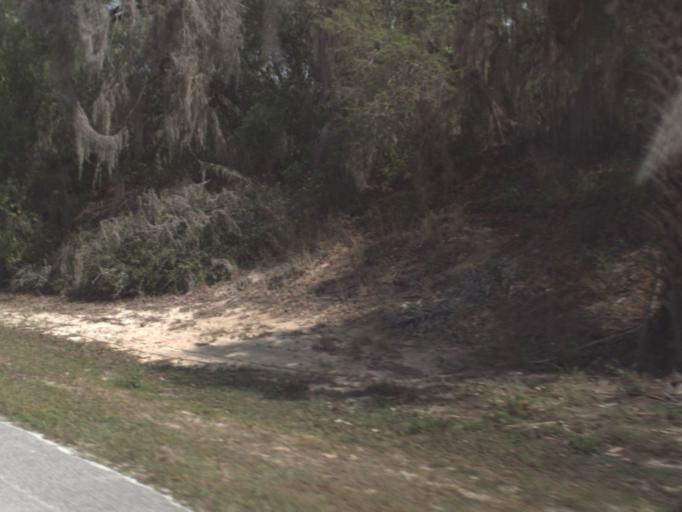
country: US
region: Florida
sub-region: Lake County
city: Astor
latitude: 29.2786
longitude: -81.6481
